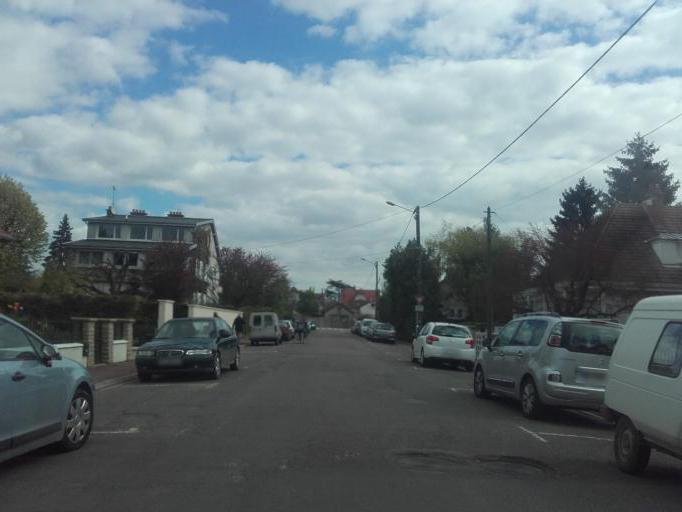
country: FR
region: Bourgogne
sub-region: Departement de la Cote-d'Or
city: Nuits-Saint-Georges
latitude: 47.1356
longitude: 4.9519
